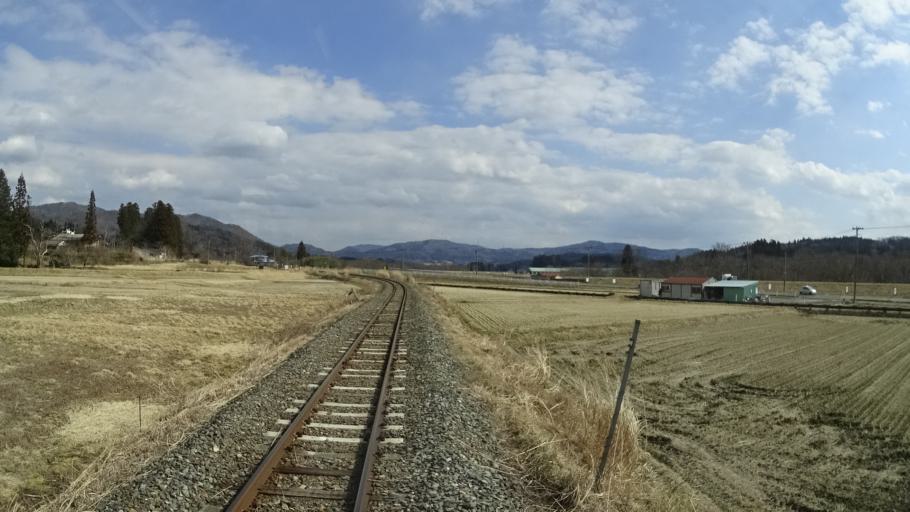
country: JP
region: Iwate
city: Hanamaki
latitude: 39.3785
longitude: 141.2403
